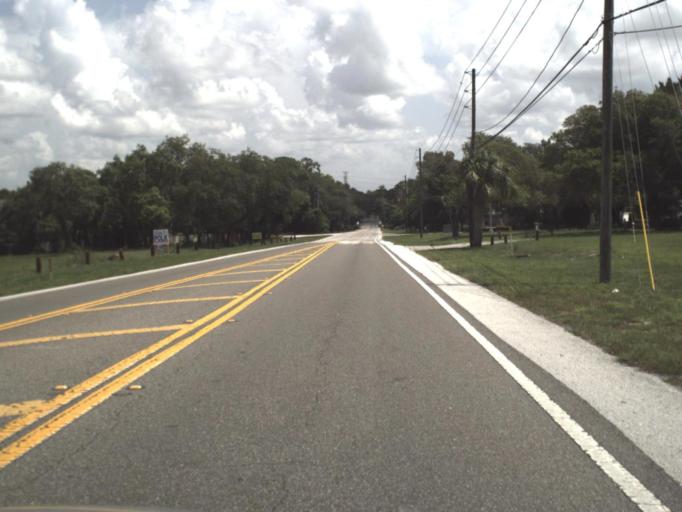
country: US
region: Florida
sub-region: Pinellas County
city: Safety Harbor
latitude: 27.9741
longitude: -82.7433
